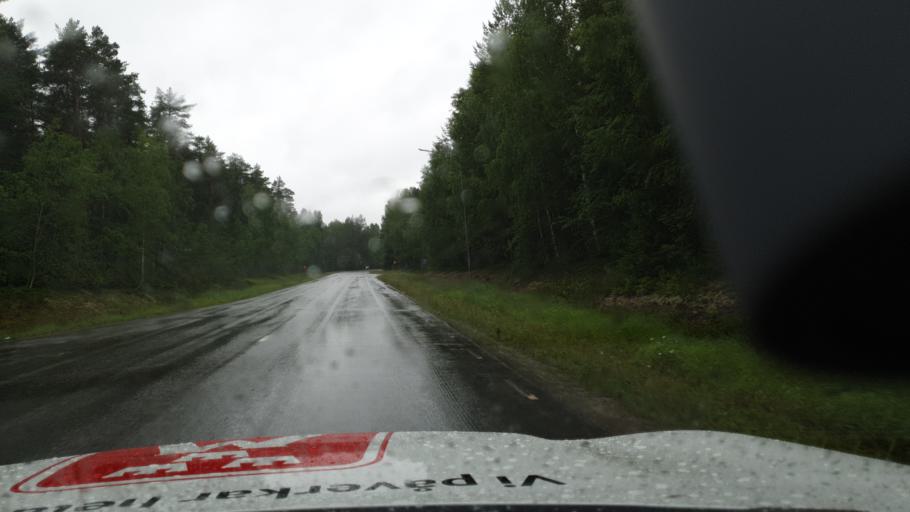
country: SE
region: Vaesterbotten
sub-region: Nordmalings Kommun
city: Nordmaling
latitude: 63.5484
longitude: 19.4076
